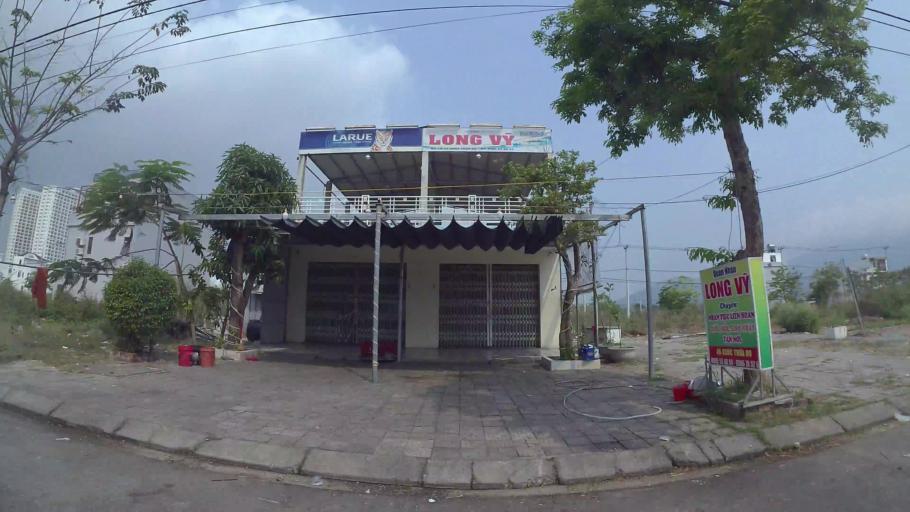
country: VN
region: Da Nang
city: Da Nang
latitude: 16.0975
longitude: 108.2291
